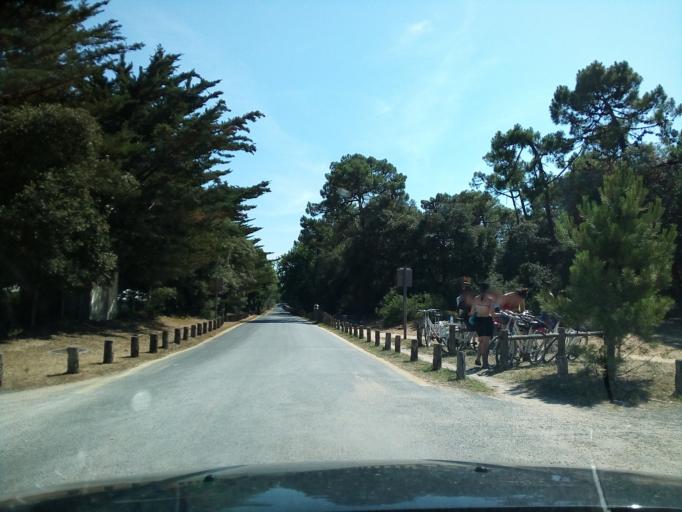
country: FR
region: Poitou-Charentes
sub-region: Departement de la Charente-Maritime
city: Boyard-Ville
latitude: 45.9874
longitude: -1.2934
